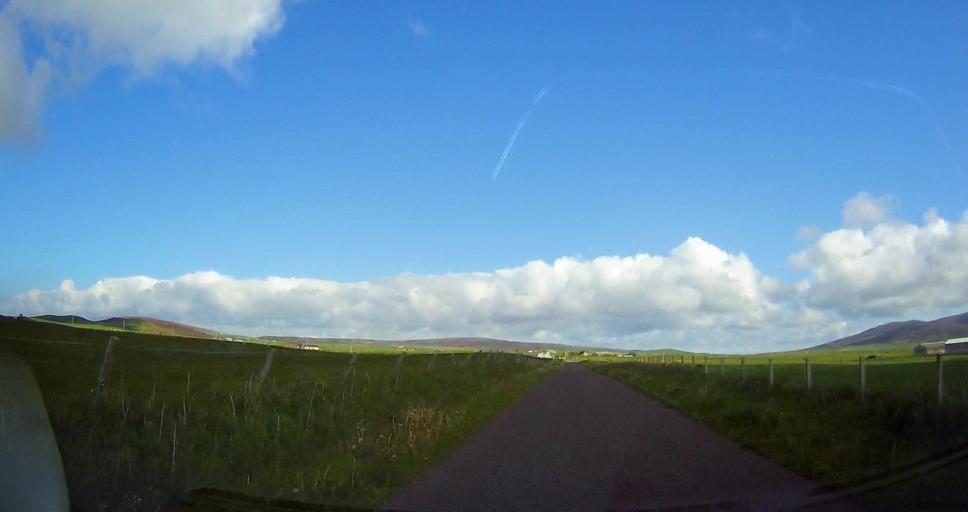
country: GB
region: Scotland
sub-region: Orkney Islands
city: Stromness
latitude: 58.9995
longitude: -3.1707
